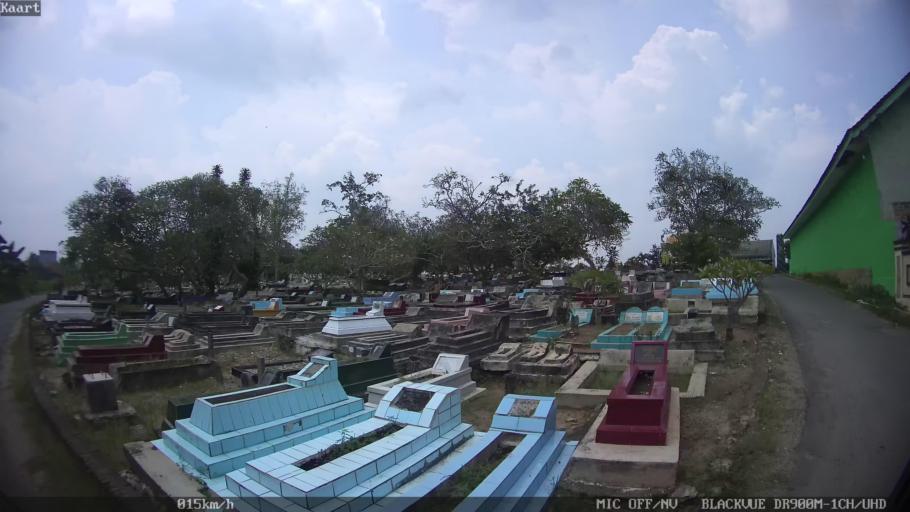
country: ID
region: Lampung
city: Pringsewu
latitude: -5.3481
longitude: 104.9700
